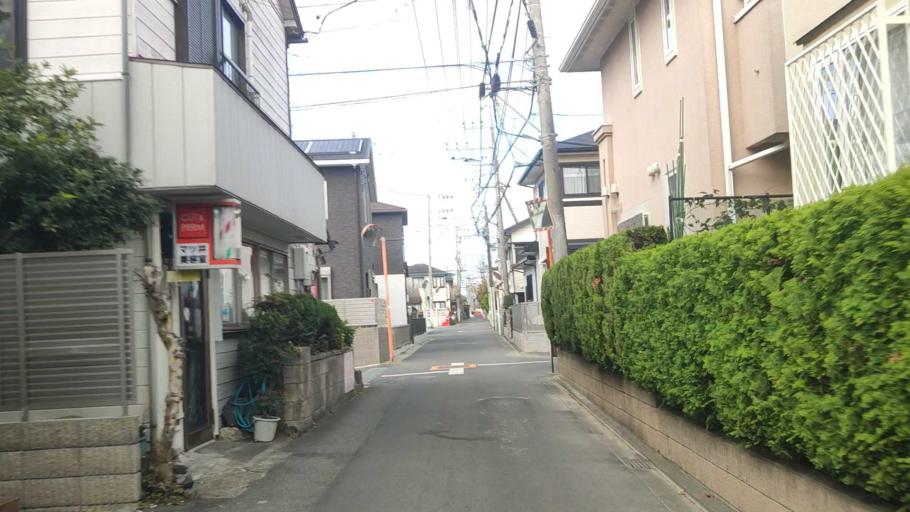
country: JP
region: Kanagawa
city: Minami-rinkan
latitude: 35.4893
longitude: 139.4380
